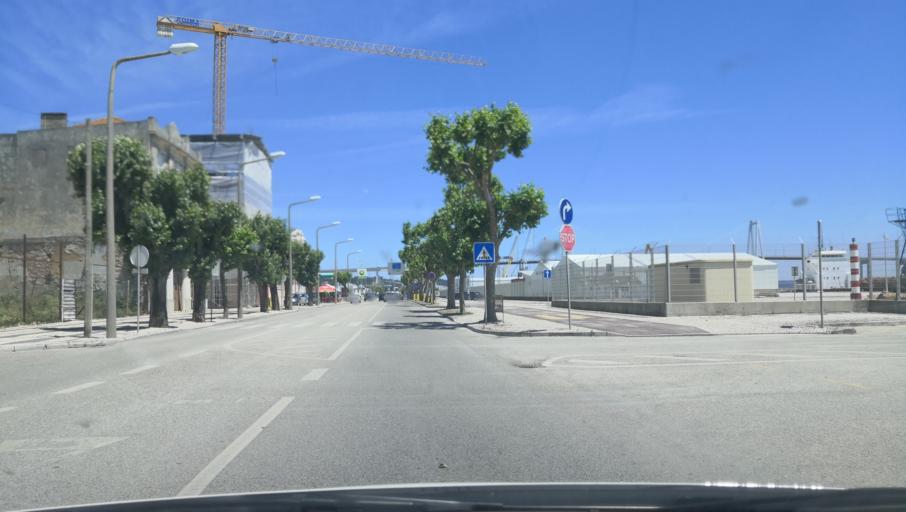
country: PT
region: Coimbra
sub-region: Figueira da Foz
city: Figueira da Foz
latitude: 40.1480
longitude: -8.8520
